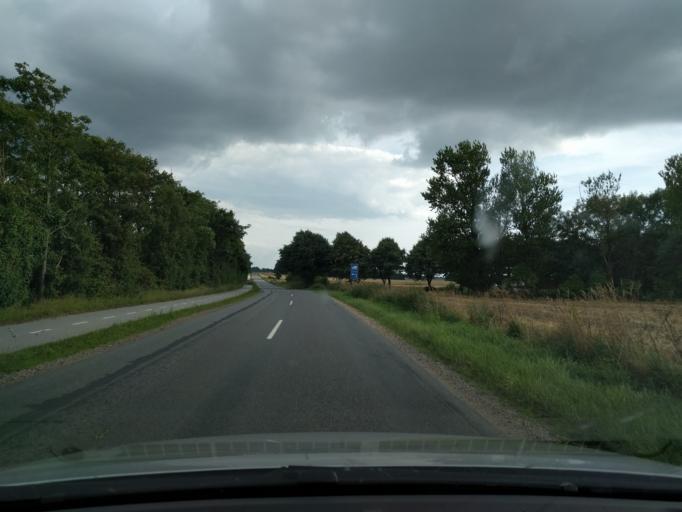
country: DK
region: Central Jutland
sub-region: Herning Kommune
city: Snejbjerg
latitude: 56.1073
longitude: 8.9082
